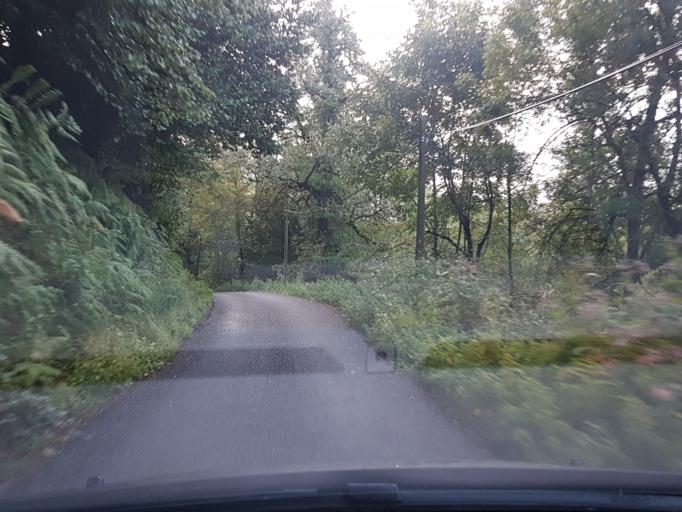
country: FR
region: Midi-Pyrenees
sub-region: Departement de l'Ariege
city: Montjoie-en-Couserans
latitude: 42.9034
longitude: 1.3588
